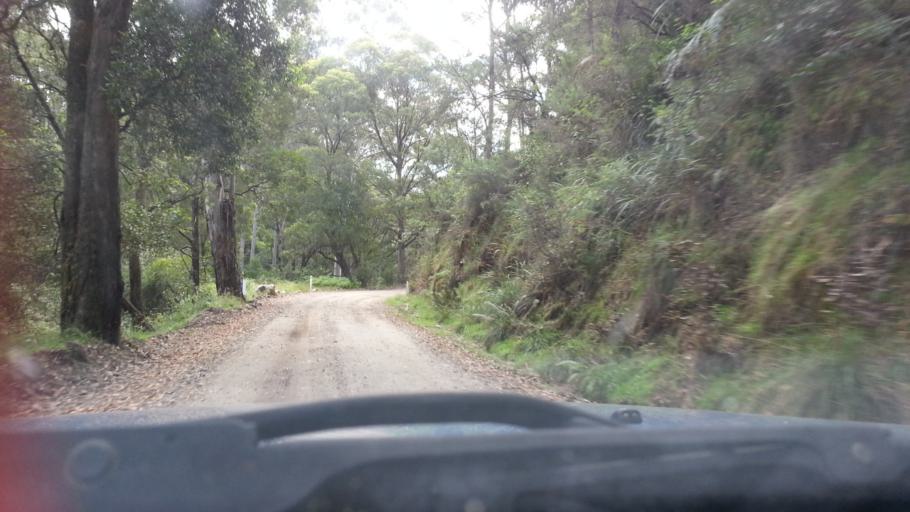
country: AU
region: Victoria
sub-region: Alpine
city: Mount Beauty
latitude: -36.6993
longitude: 147.2552
